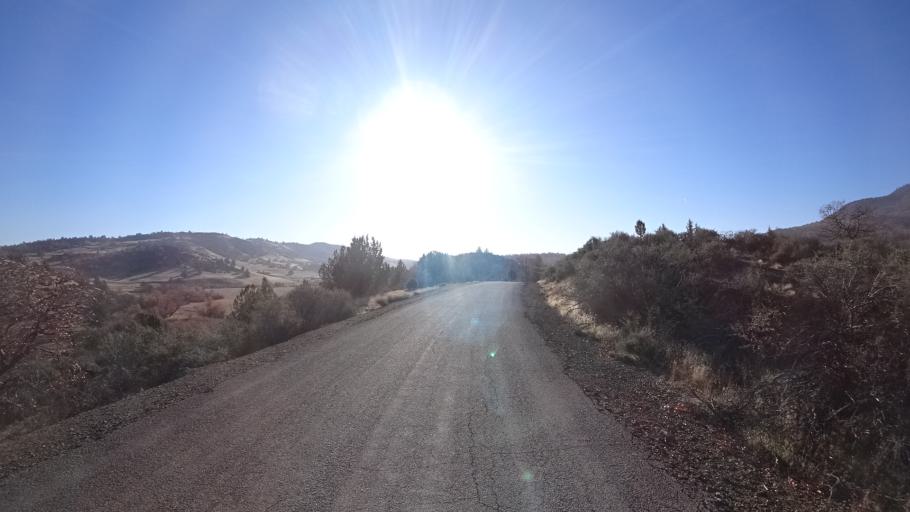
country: US
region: California
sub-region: Siskiyou County
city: Montague
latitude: 41.8924
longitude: -122.4906
